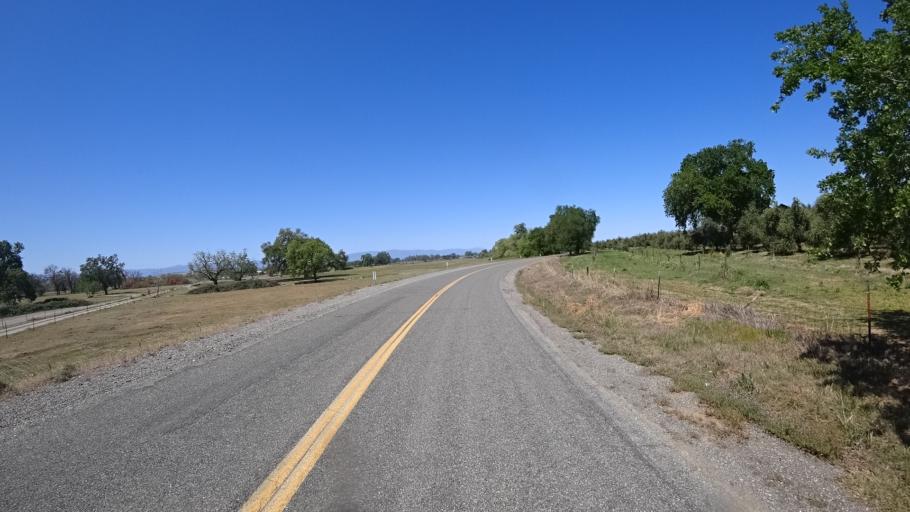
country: US
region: California
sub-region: Glenn County
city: Orland
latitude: 39.7842
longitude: -122.2167
